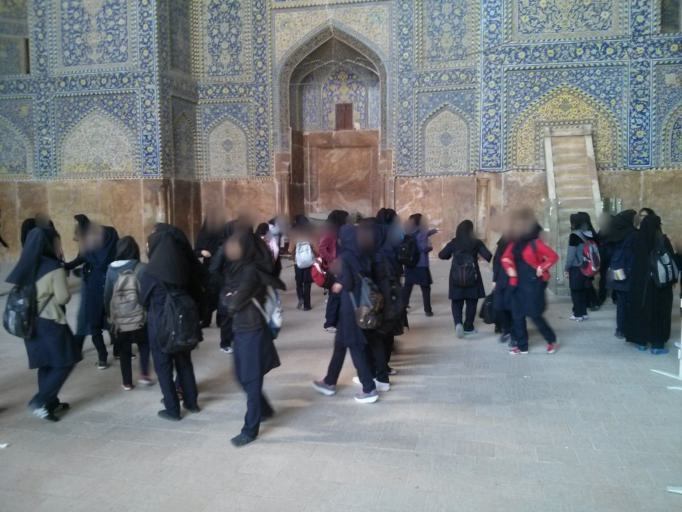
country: IR
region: Isfahan
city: Isfahan
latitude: 32.6559
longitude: 51.6777
